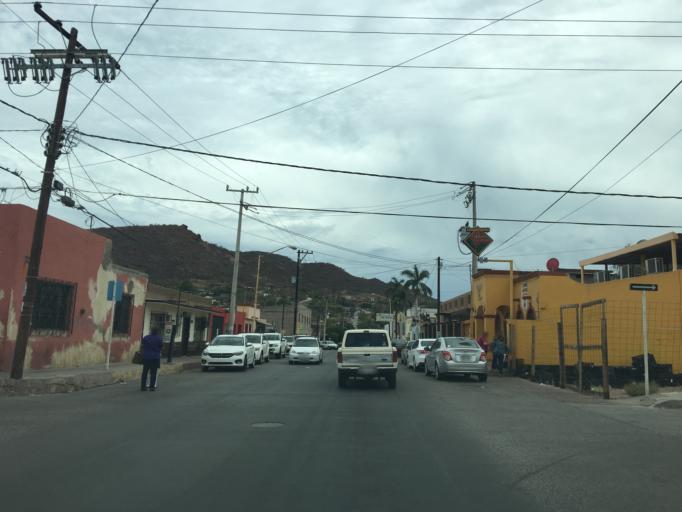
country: MX
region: Sonora
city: Heroica Guaymas
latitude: 27.9195
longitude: -110.8989
